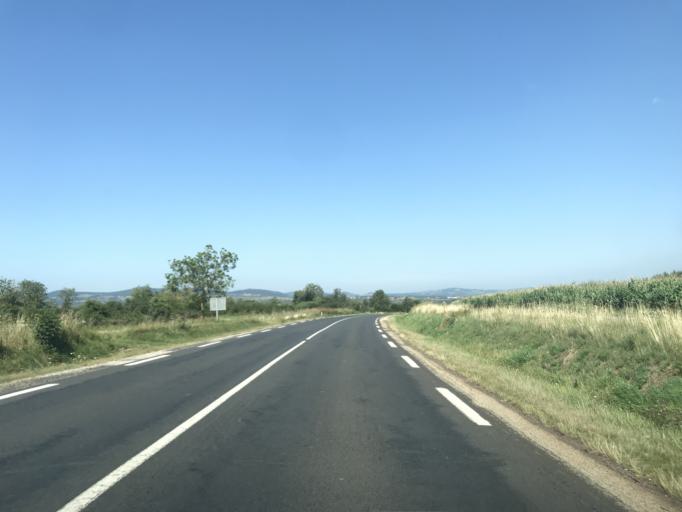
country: FR
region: Auvergne
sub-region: Departement de la Haute-Loire
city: Cussac-sur-Loire
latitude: 44.9753
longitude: 3.8340
